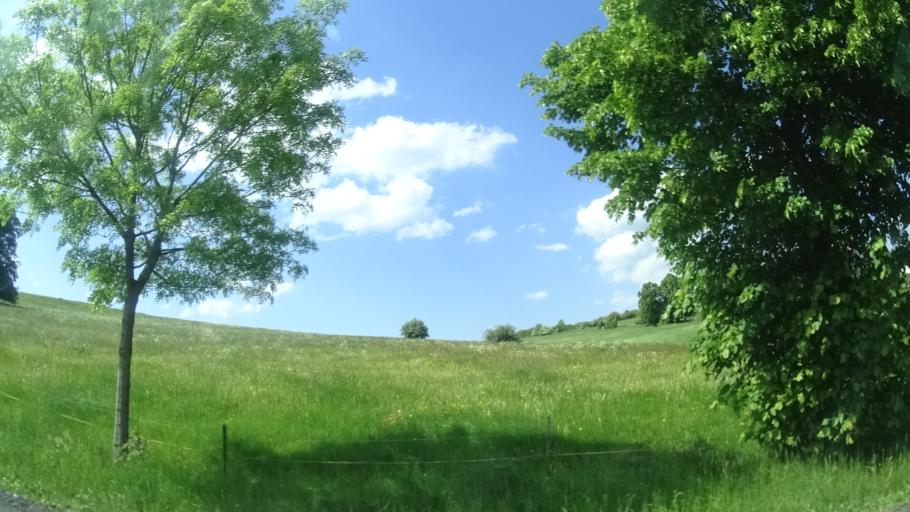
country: DE
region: Thuringia
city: Andenhausen
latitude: 50.6689
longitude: 10.0676
